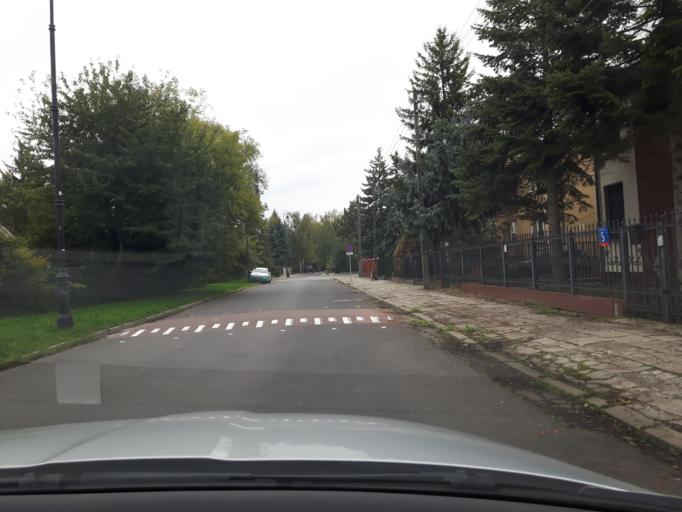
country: PL
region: Masovian Voivodeship
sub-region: Warszawa
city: Mokotow
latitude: 52.1872
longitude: 21.0348
